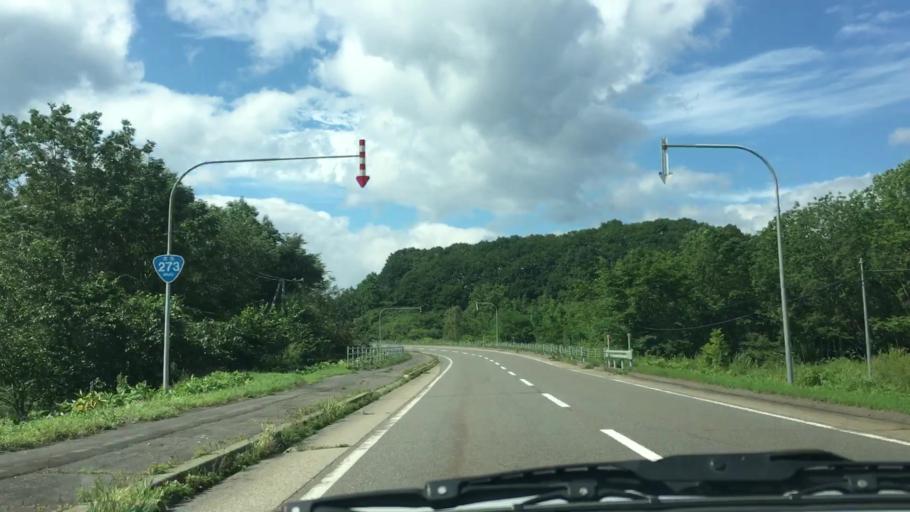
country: JP
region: Hokkaido
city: Otofuke
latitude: 43.3338
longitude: 143.2906
